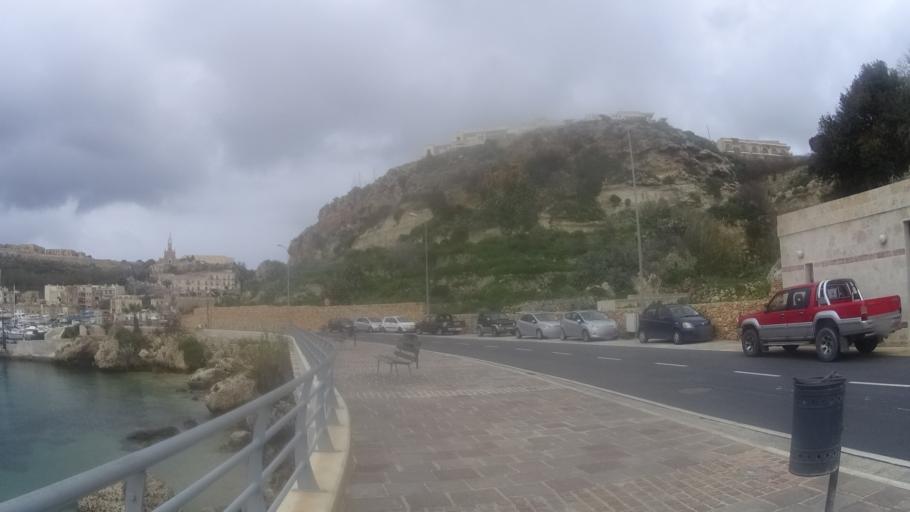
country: MT
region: Ghajnsielem
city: Mgarr
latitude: 36.0268
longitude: 14.2992
